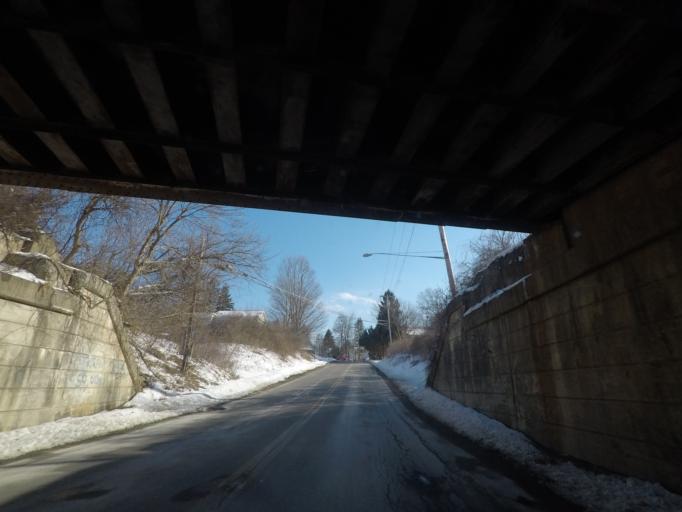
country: US
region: New York
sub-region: Saratoga County
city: Stillwater
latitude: 42.9156
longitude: -73.5139
